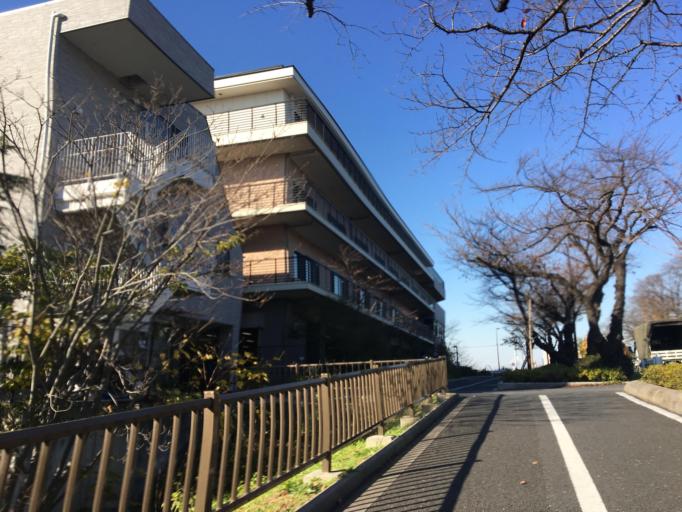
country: JP
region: Tokyo
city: Urayasu
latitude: 35.7010
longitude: 139.9169
